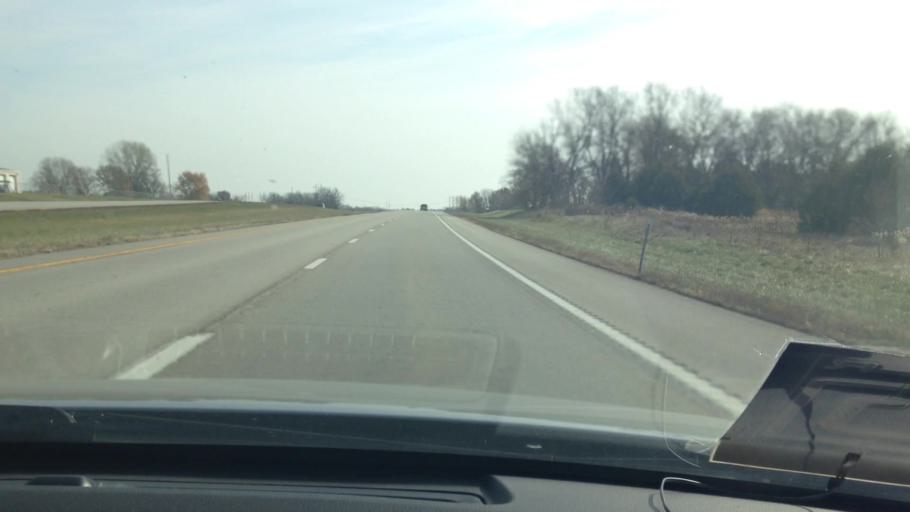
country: US
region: Missouri
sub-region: Cass County
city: Garden City
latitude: 38.5995
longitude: -94.2582
